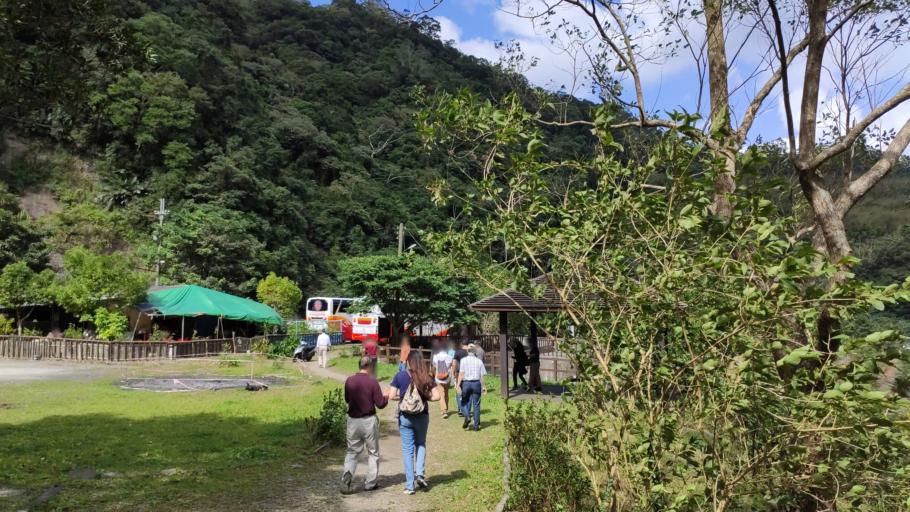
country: TW
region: Taiwan
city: Daxi
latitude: 24.8357
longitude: 121.4452
